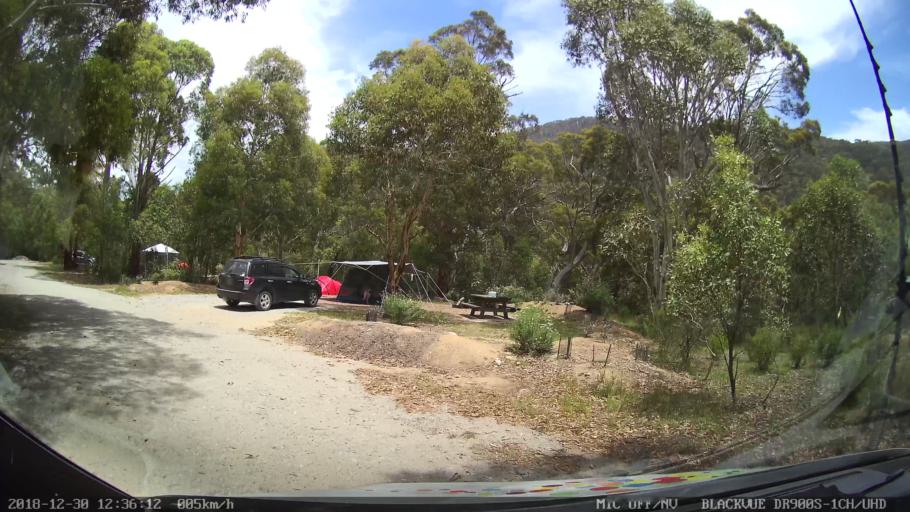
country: AU
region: New South Wales
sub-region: Snowy River
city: Jindabyne
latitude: -36.3222
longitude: 148.4640
